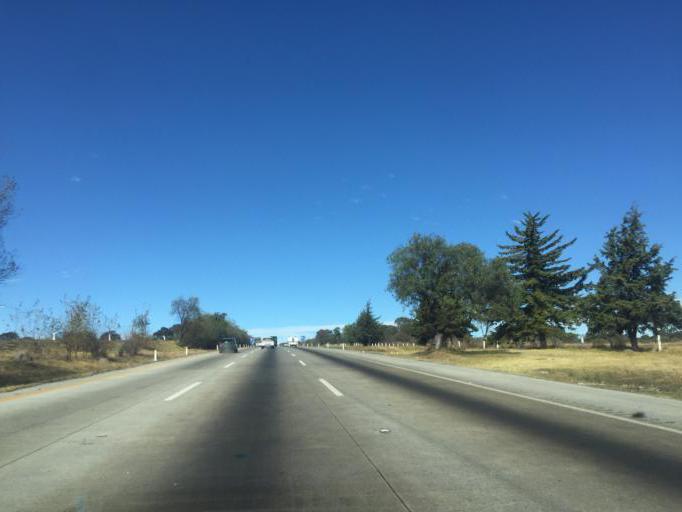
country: MX
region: Mexico
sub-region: Jilotepec
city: La Comunidad
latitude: 20.0331
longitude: -99.5531
